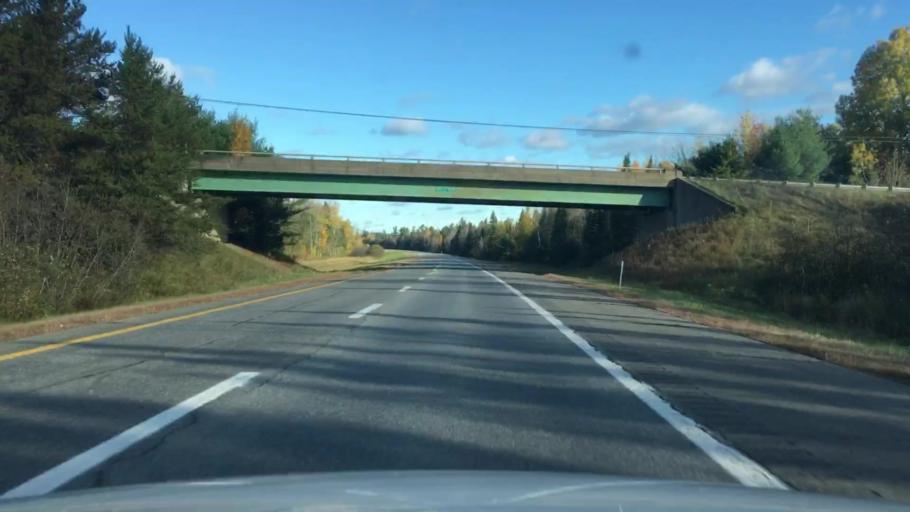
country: US
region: Maine
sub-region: Penobscot County
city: Greenbush
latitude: 45.0516
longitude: -68.6872
